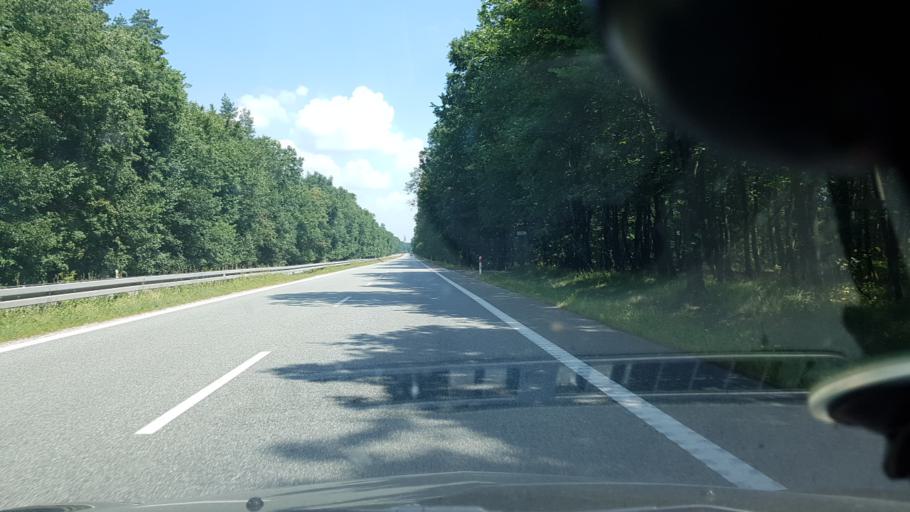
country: PL
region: Silesian Voivodeship
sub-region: Zory
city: Zory
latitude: 50.0693
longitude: 18.7352
